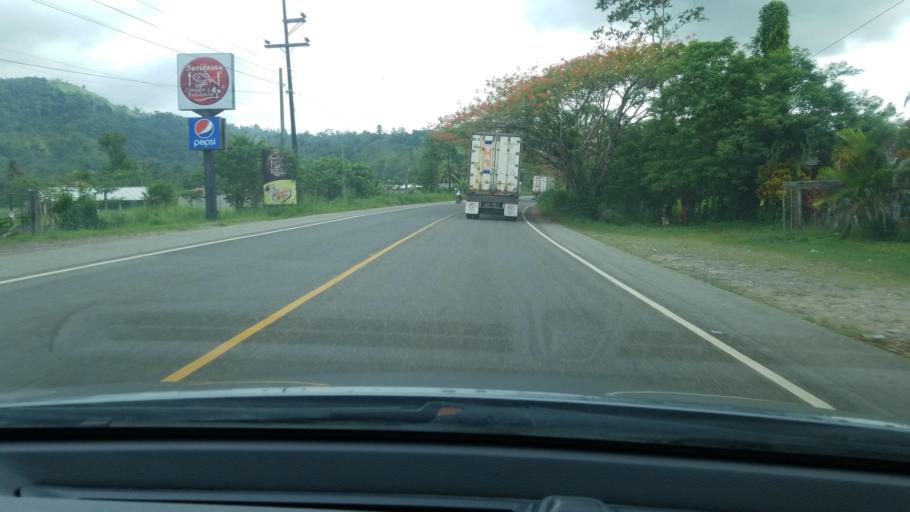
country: HN
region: Cortes
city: Potrerillos
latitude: 15.5875
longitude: -88.3300
